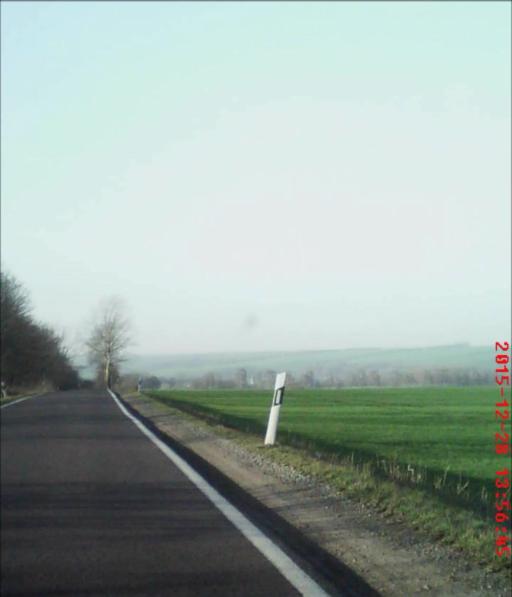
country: DE
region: Thuringia
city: Bad Sulza
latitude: 51.0630
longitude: 11.6226
